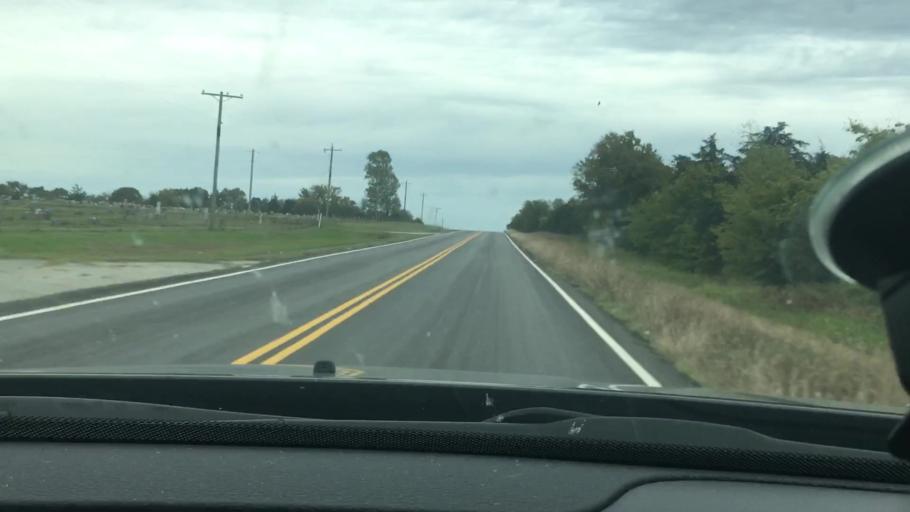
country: US
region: Oklahoma
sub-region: Coal County
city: Coalgate
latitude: 34.3884
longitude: -96.4245
